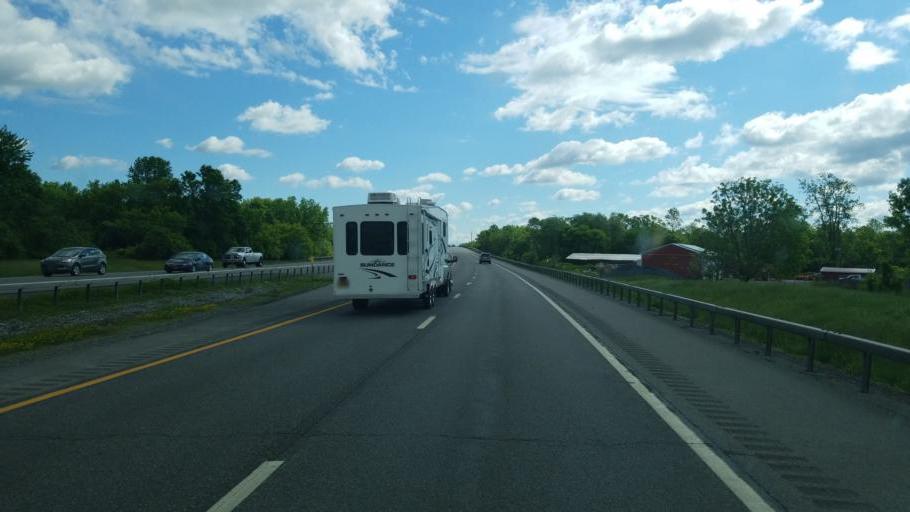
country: US
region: New York
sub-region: Cayuga County
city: Port Byron
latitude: 43.0395
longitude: -76.6306
